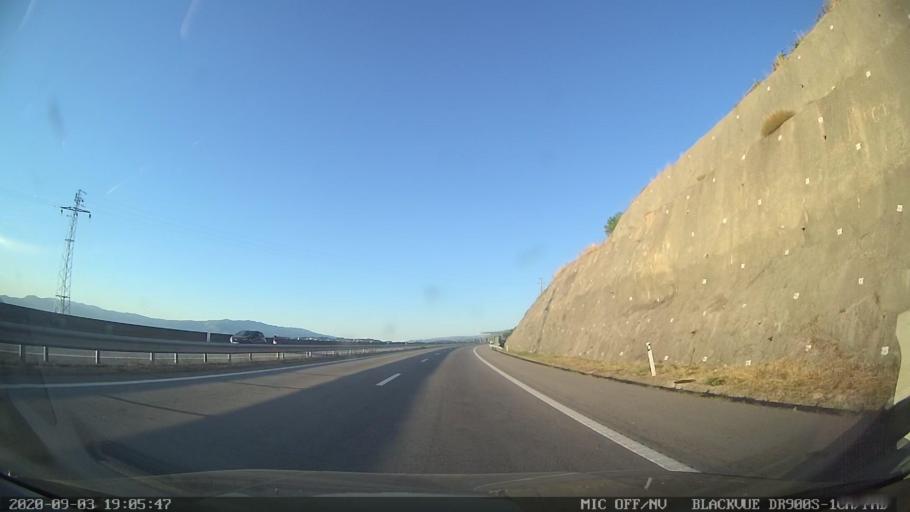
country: PT
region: Vila Real
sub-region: Santa Marta de Penaguiao
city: Santa Marta de Penaguiao
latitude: 41.2279
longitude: -7.7362
